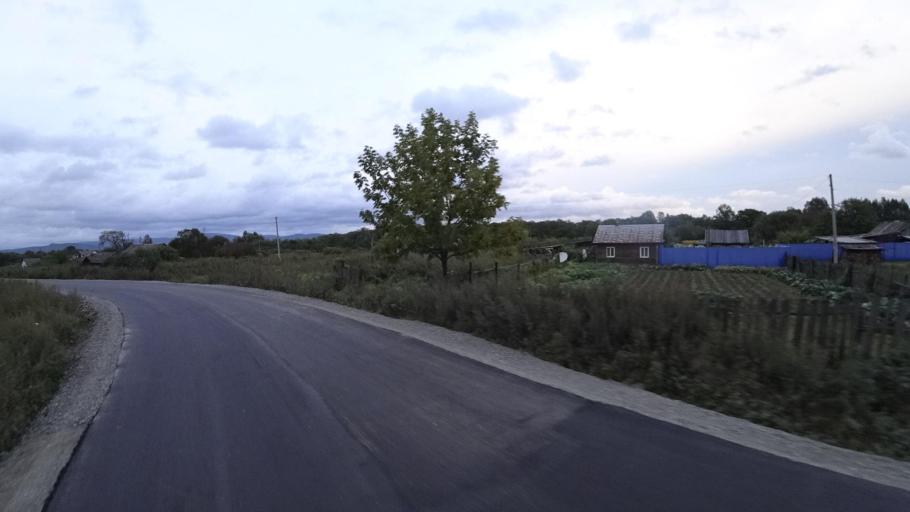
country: RU
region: Jewish Autonomous Oblast
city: Izvestkovyy
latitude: 48.9899
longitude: 131.5473
